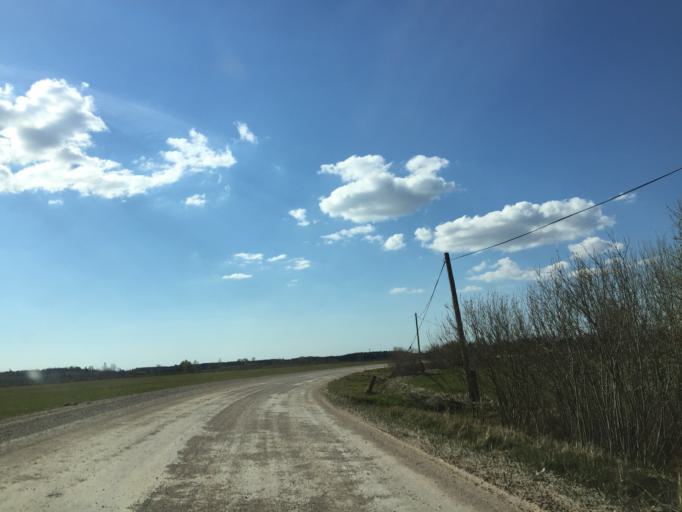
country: LV
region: Saulkrastu
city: Saulkrasti
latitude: 57.3462
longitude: 24.5809
